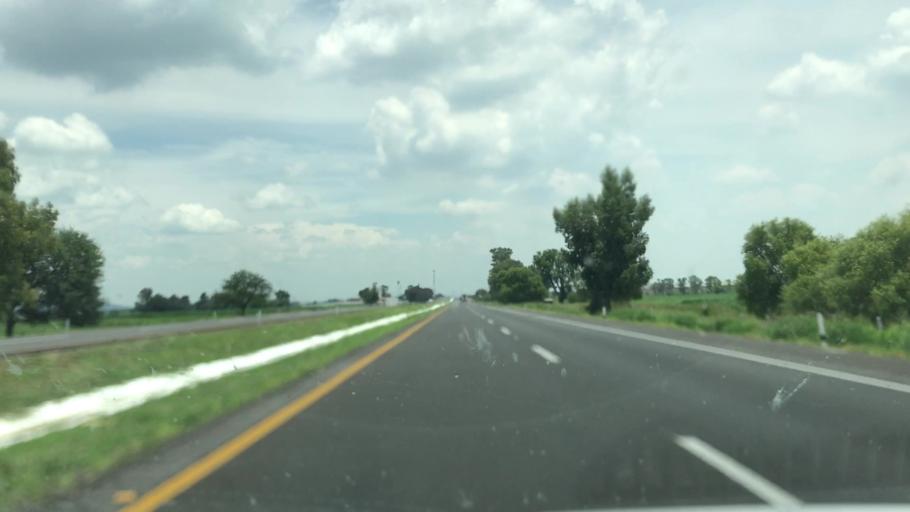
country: MX
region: Guanajuato
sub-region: Salamanca
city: San Vicente de Flores
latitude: 20.6271
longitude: -101.2447
